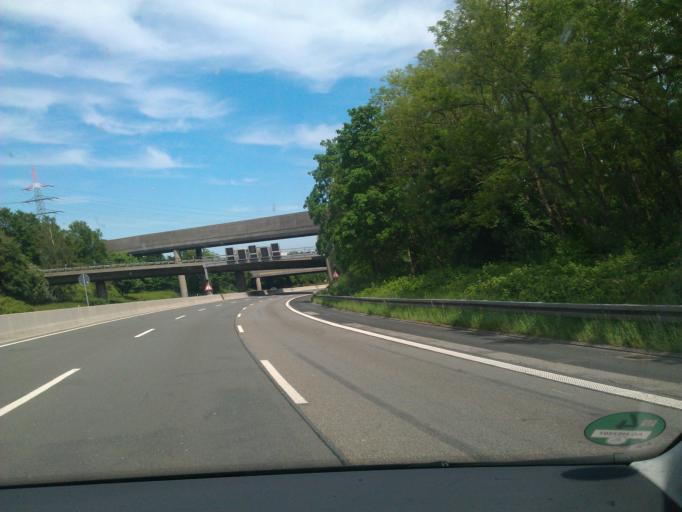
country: DE
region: North Rhine-Westphalia
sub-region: Regierungsbezirk Dusseldorf
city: Dusseldorf
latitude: 51.1902
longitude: 6.7778
